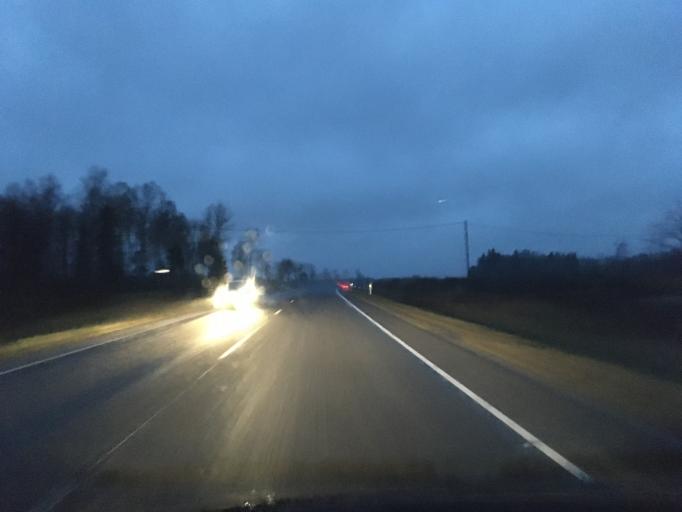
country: EE
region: Harju
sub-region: Nissi vald
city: Turba
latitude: 58.9769
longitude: 24.0588
